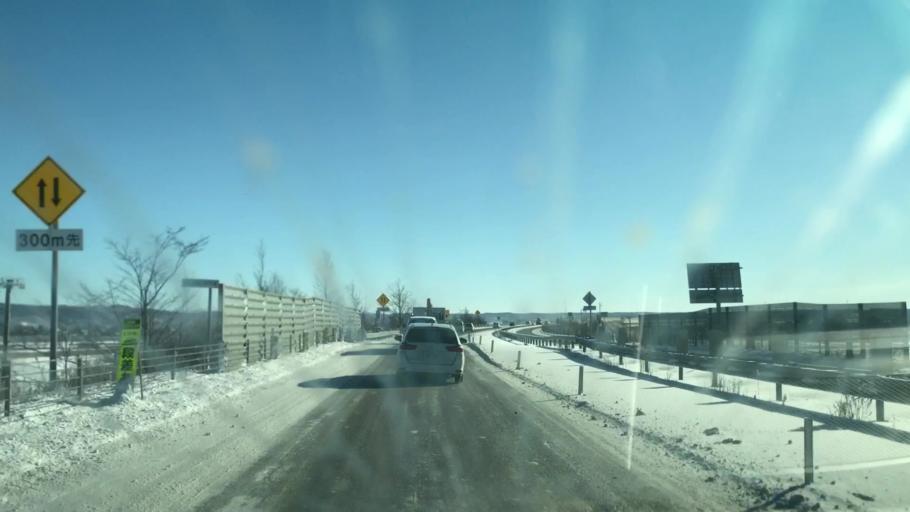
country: JP
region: Hokkaido
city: Tomakomai
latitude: 42.5865
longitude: 141.9380
